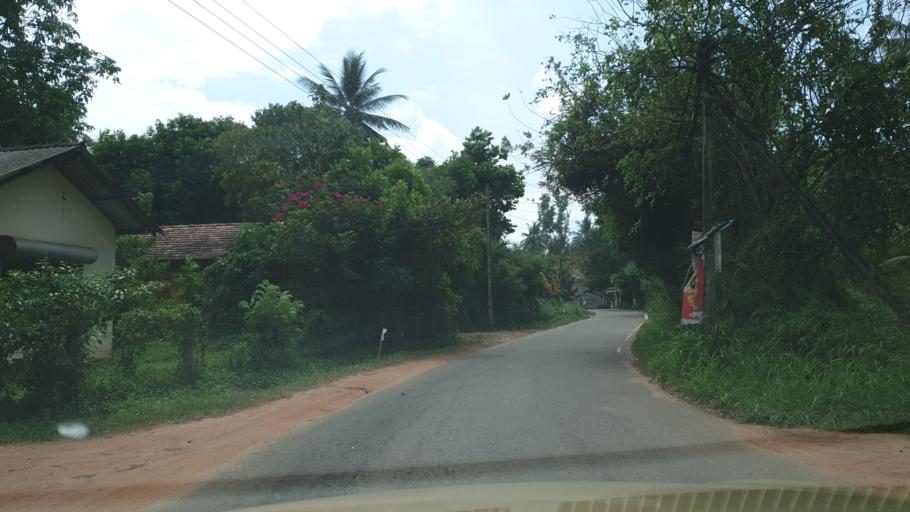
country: LK
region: North Western
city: Kuliyapitiya
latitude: 7.3635
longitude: 79.9669
